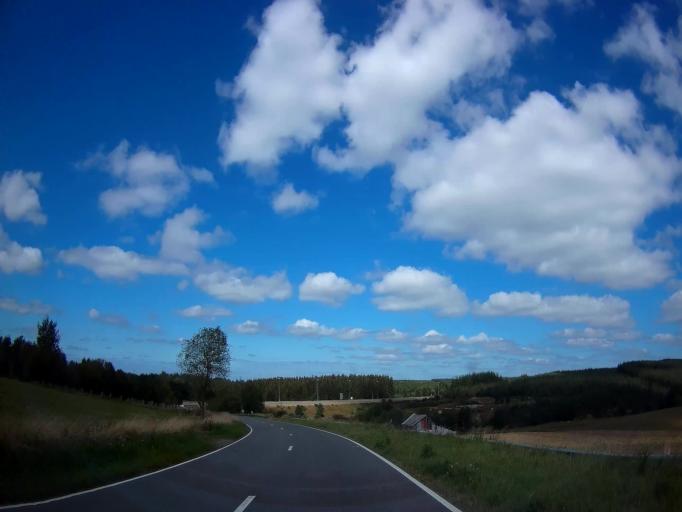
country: BE
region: Wallonia
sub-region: Province du Luxembourg
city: Bastogne
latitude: 50.0279
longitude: 5.7033
